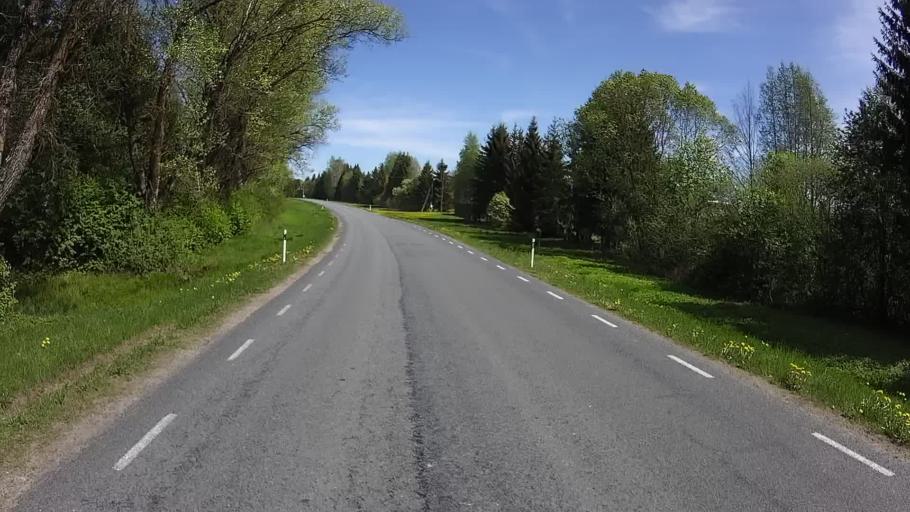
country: LV
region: Apes Novads
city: Ape
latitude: 57.6072
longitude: 26.5634
